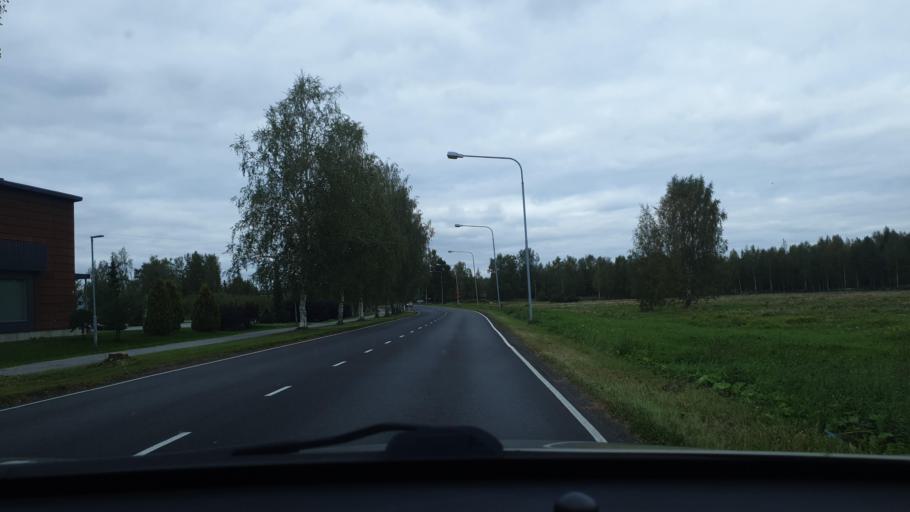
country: FI
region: Ostrobothnia
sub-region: Vaasa
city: Teeriniemi
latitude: 63.0870
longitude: 21.6990
